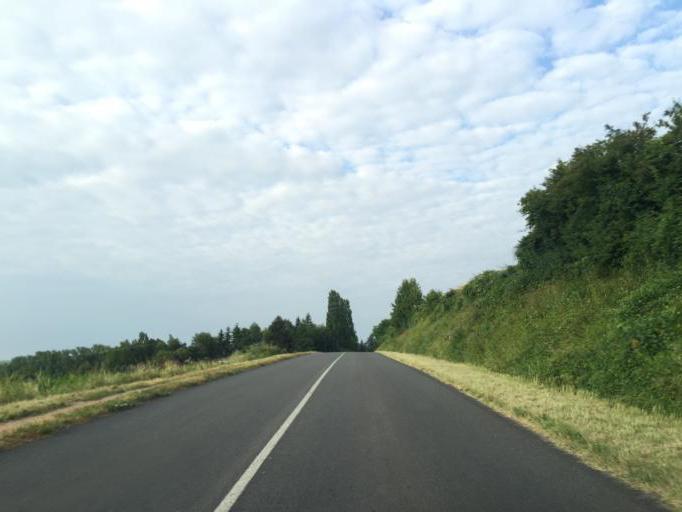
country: FR
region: Auvergne
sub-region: Departement de l'Allier
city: Saint-Germain-des-Fosses
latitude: 46.1856
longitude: 3.4246
